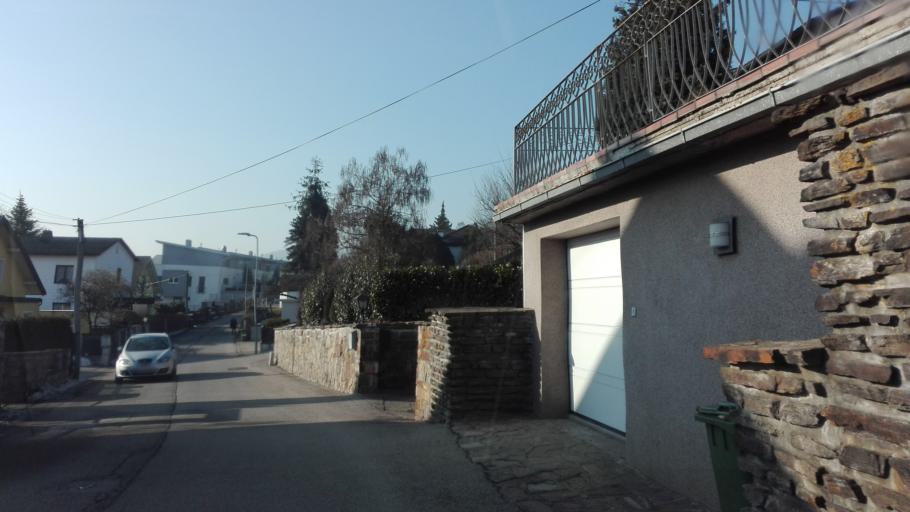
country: AT
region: Upper Austria
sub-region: Politischer Bezirk Linz-Land
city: Leonding
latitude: 48.2816
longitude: 14.2640
